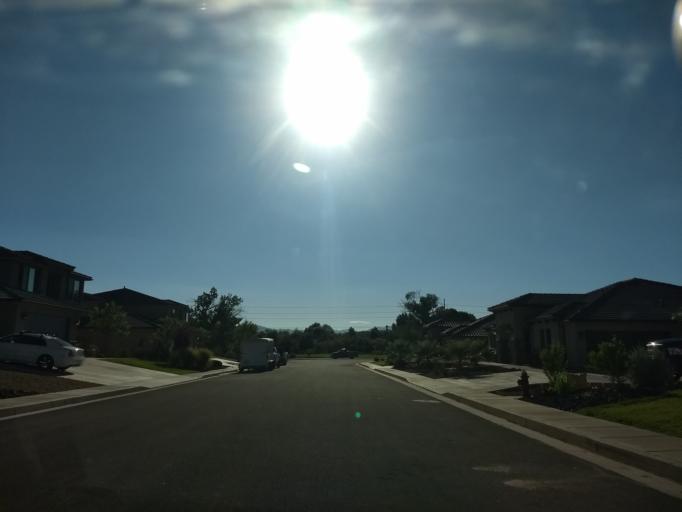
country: US
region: Utah
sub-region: Washington County
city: Washington
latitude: 37.1204
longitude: -113.5066
